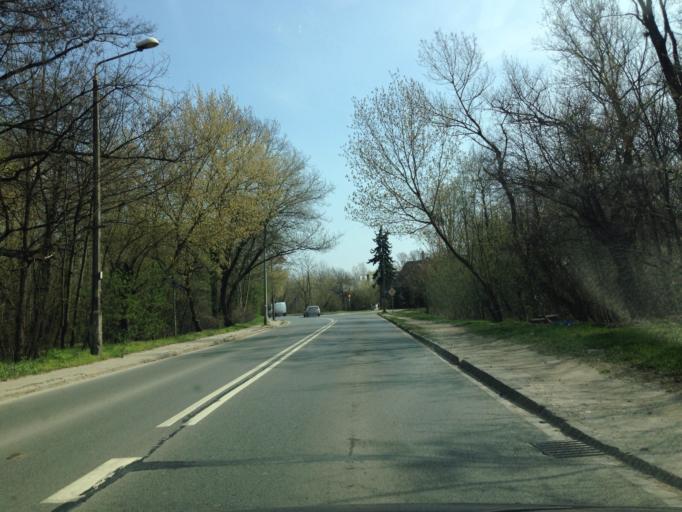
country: PL
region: Lower Silesian Voivodeship
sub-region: Powiat wroclawski
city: Wilczyce
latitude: 51.1138
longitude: 17.1179
